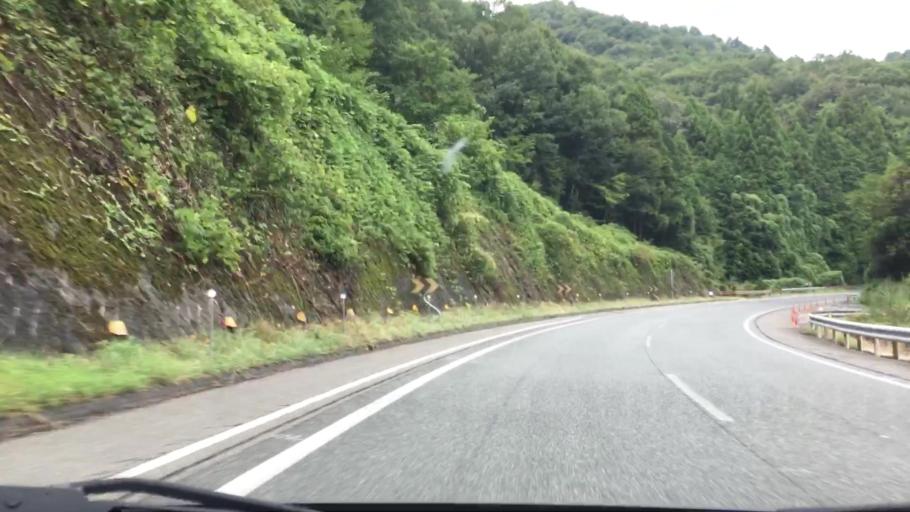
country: JP
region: Okayama
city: Niimi
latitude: 34.9867
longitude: 133.6070
